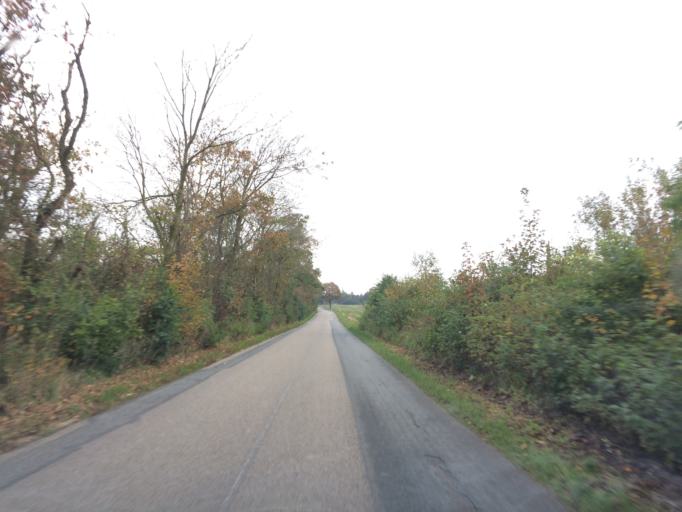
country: DK
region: Central Jutland
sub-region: Holstebro Kommune
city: Holstebro
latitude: 56.3428
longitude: 8.4991
